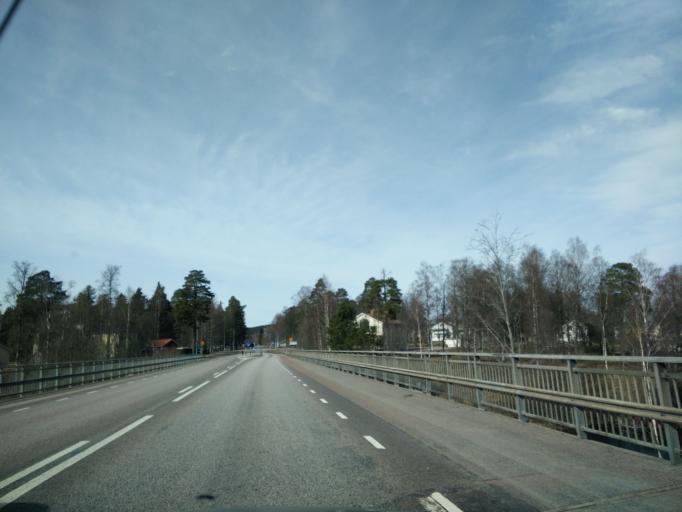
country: SE
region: Vaermland
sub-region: Hagfors Kommun
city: Hagfors
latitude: 60.0195
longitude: 13.6235
